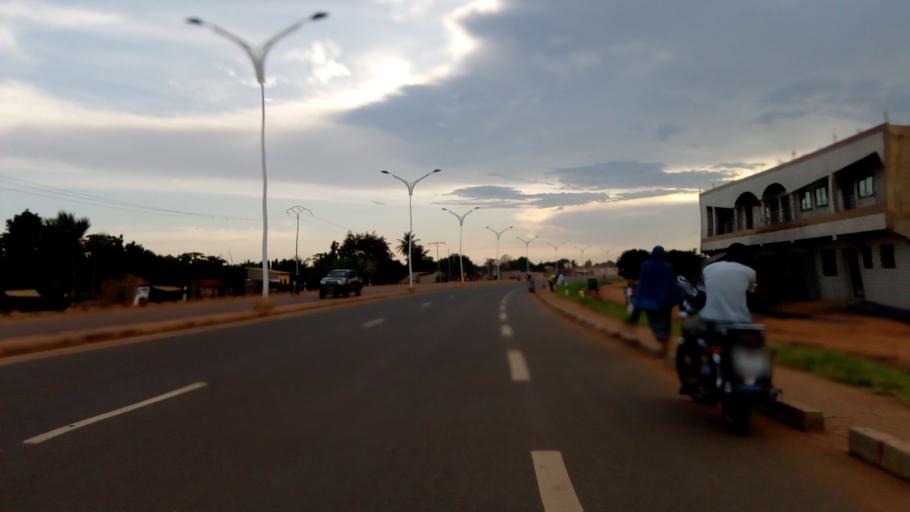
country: TG
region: Maritime
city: Lome
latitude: 6.2658
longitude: 1.1475
